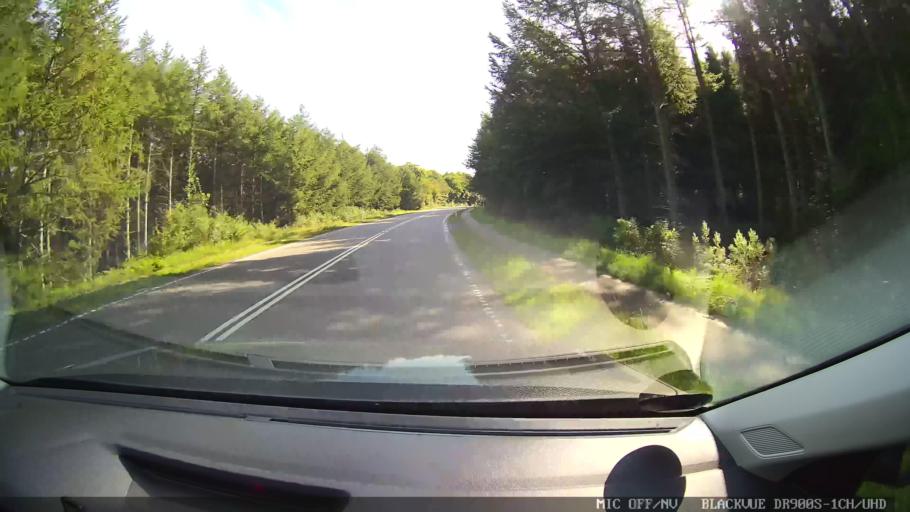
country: DK
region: North Denmark
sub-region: Mariagerfjord Kommune
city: Arden
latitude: 56.7747
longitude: 9.7968
